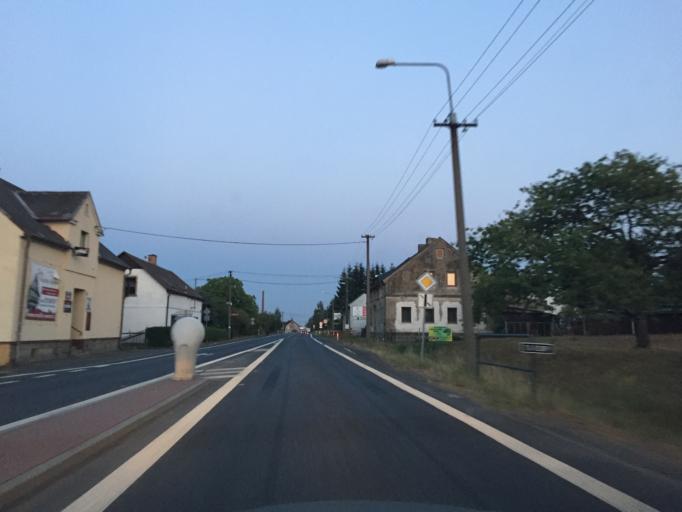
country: CZ
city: Cvikov
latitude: 50.7831
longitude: 14.6169
